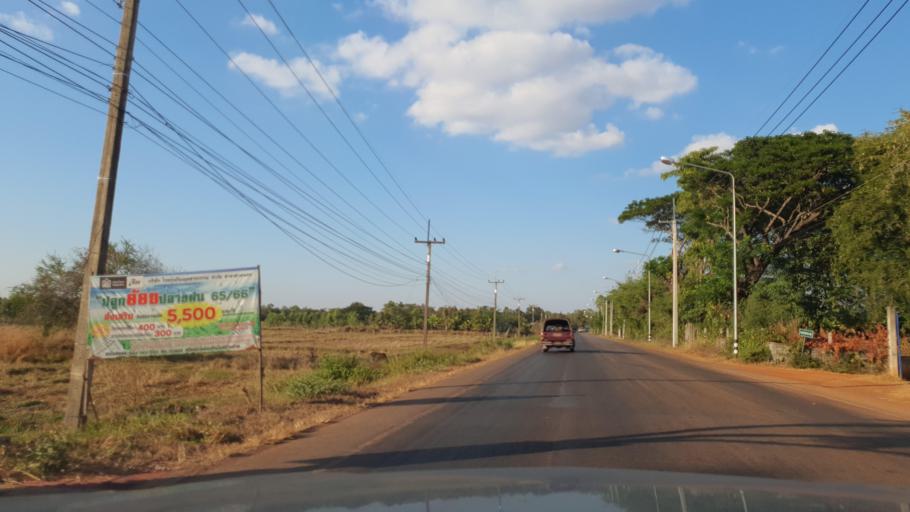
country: TH
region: Sakon Nakhon
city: Phon Na Kaeo
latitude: 17.2660
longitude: 104.1916
